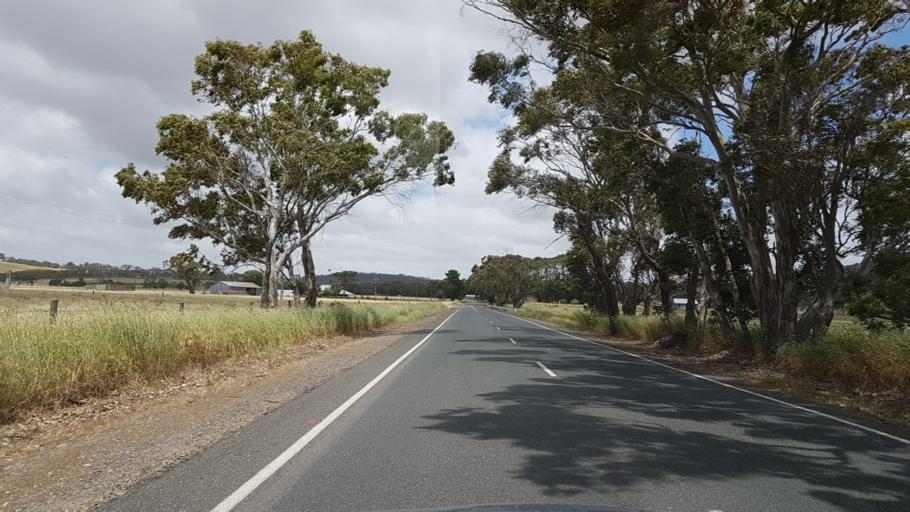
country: AU
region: South Australia
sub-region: Onkaparinga
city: Aldinga
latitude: -35.3884
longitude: 138.4994
